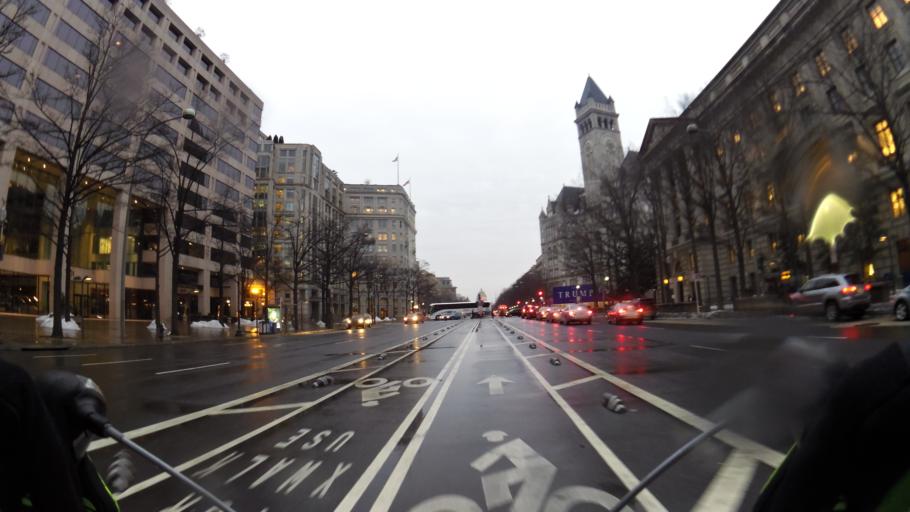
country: US
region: Washington, D.C.
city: Washington, D.C.
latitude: 38.8953
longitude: -77.0291
